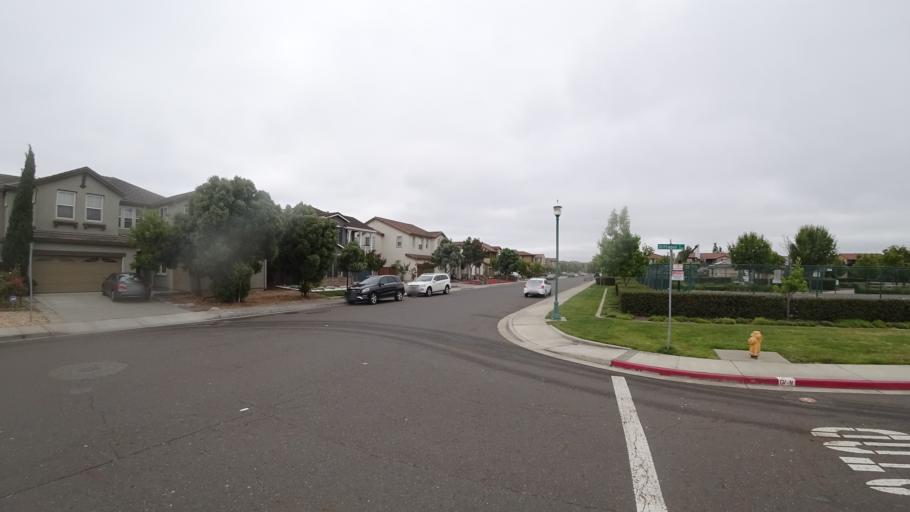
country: US
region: California
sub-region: Alameda County
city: Hayward
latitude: 37.6062
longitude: -122.0915
